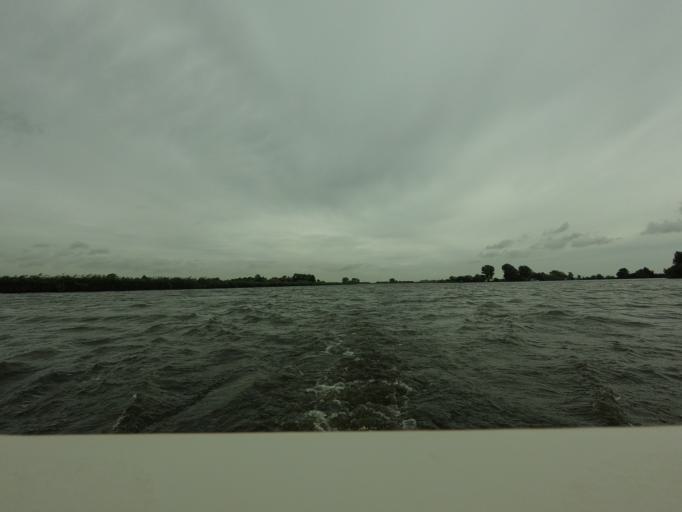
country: NL
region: Friesland
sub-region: Gemeente Boarnsterhim
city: Grou
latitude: 53.1044
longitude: 5.8539
